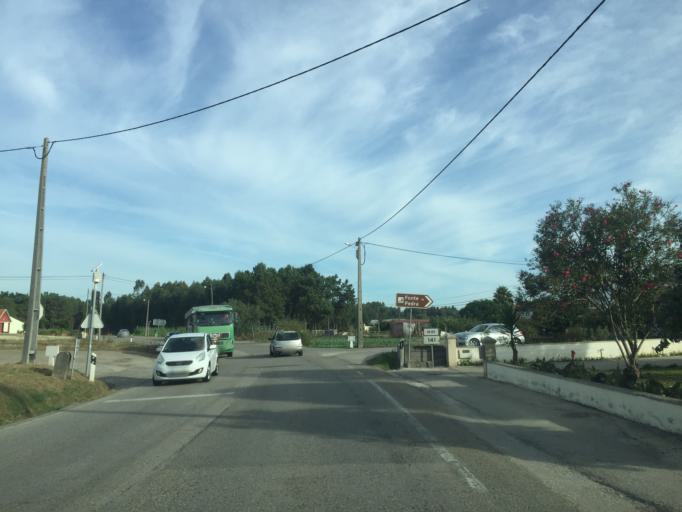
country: PT
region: Leiria
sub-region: Pombal
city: Lourical
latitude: 39.9704
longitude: -8.7927
